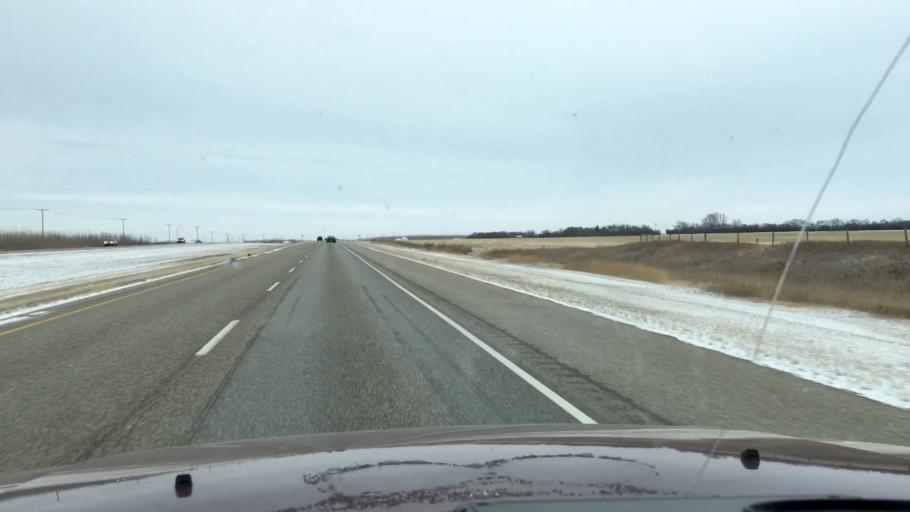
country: CA
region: Saskatchewan
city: Watrous
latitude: 51.0581
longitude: -105.8171
